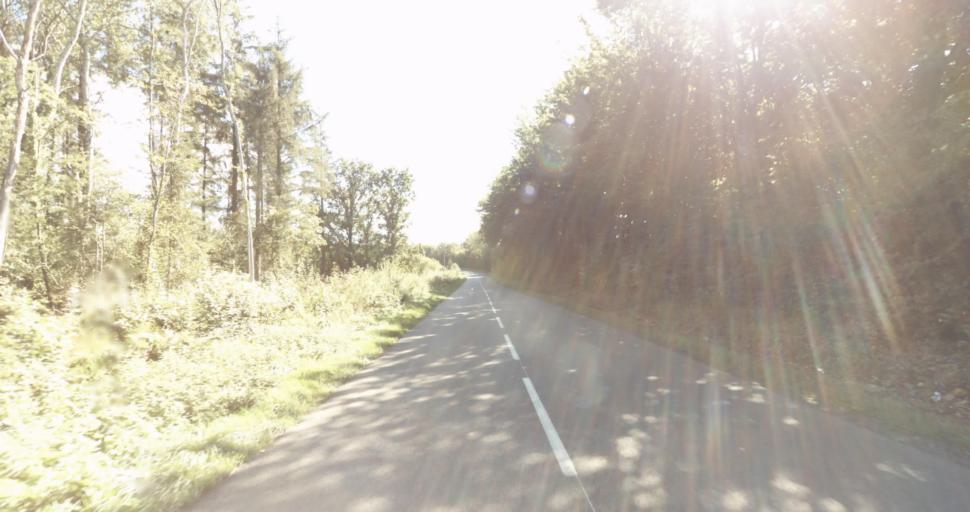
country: FR
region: Lower Normandy
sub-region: Departement de l'Orne
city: Gace
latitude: 48.7874
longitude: 0.2241
